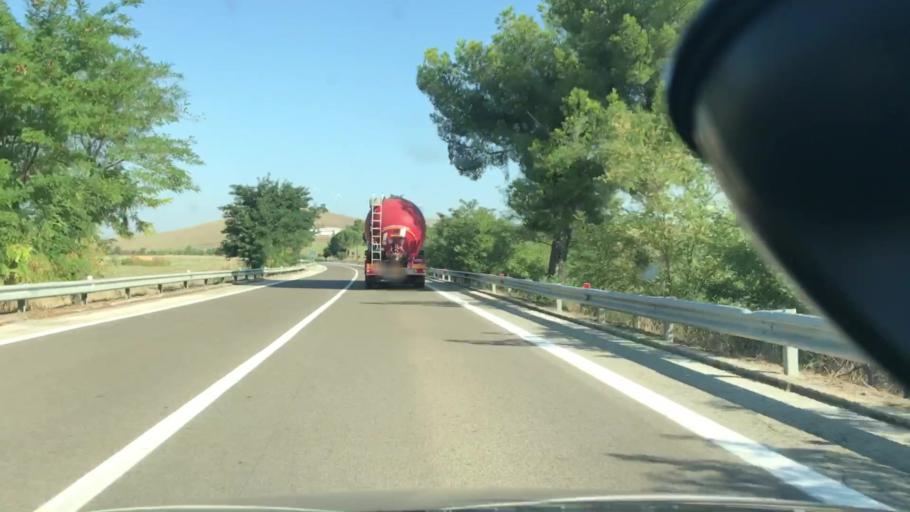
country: IT
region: Basilicate
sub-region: Provincia di Matera
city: Irsina
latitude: 40.8042
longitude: 16.2737
